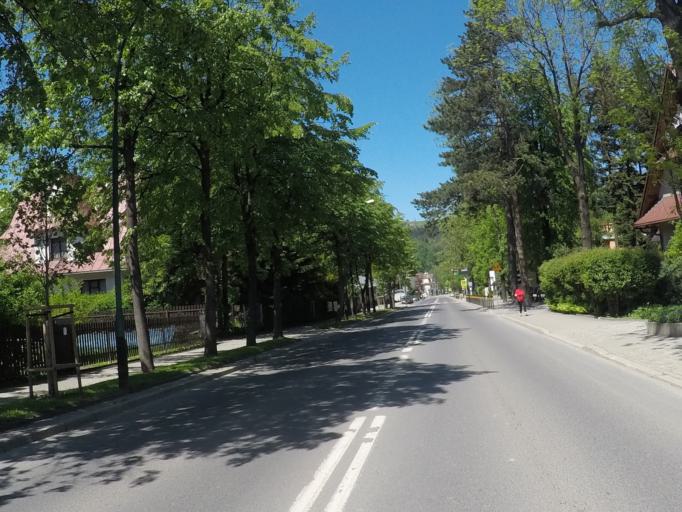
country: PL
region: Lesser Poland Voivodeship
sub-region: Powiat tatrzanski
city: Zakopane
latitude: 49.3029
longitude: 19.9602
